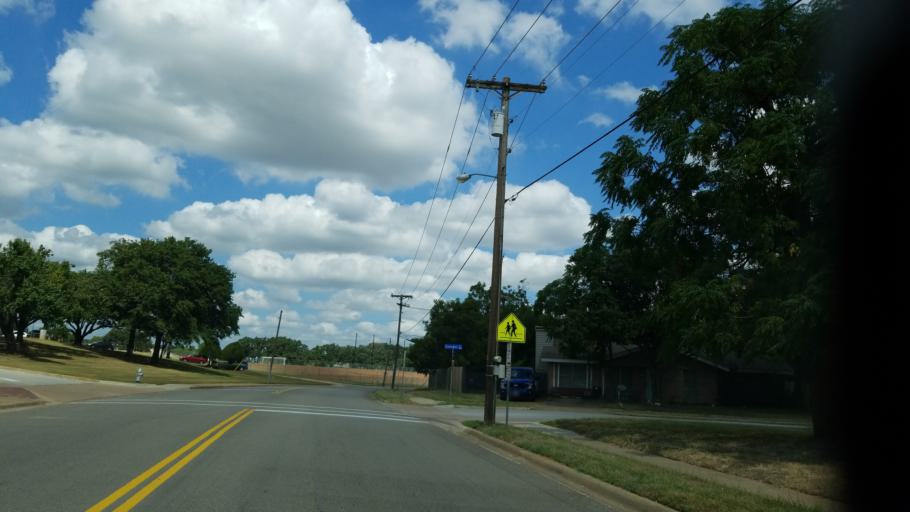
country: US
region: Texas
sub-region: Tarrant County
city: Euless
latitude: 32.8420
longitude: -97.0920
